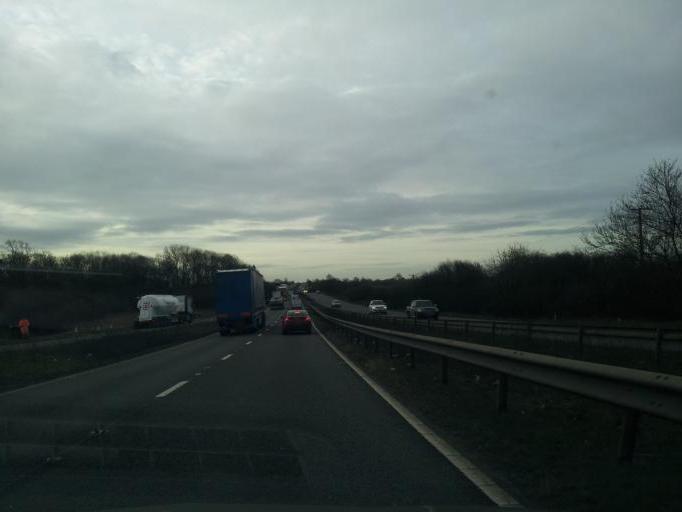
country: GB
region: England
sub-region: District of Rutland
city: Clipsham
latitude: 52.7967
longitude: -0.6106
